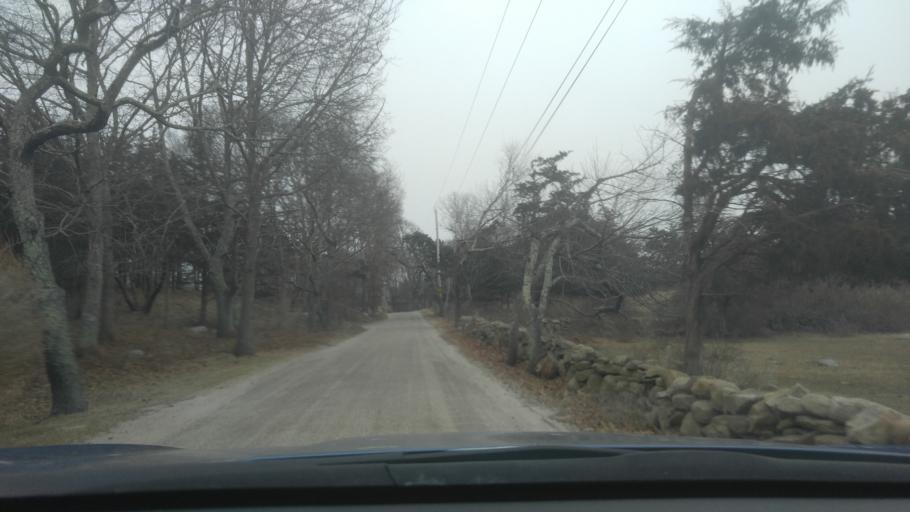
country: US
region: Rhode Island
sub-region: Washington County
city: Wakefield-Peacedale
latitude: 41.4090
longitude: -71.5219
